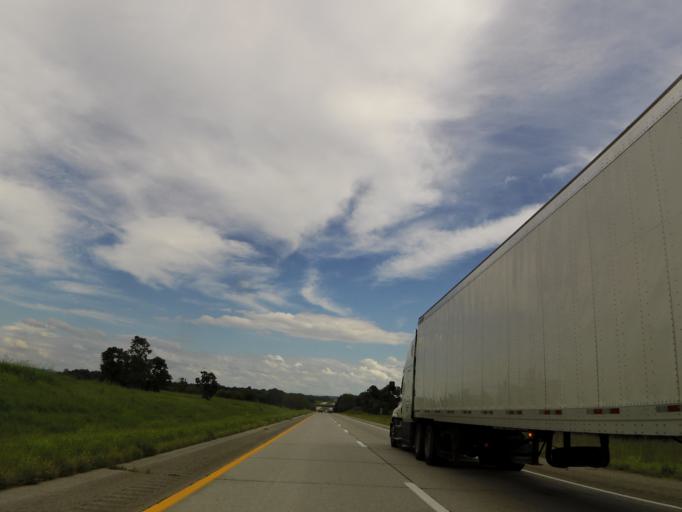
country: US
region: Kentucky
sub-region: Trigg County
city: Cadiz
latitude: 36.9385
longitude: -87.8276
